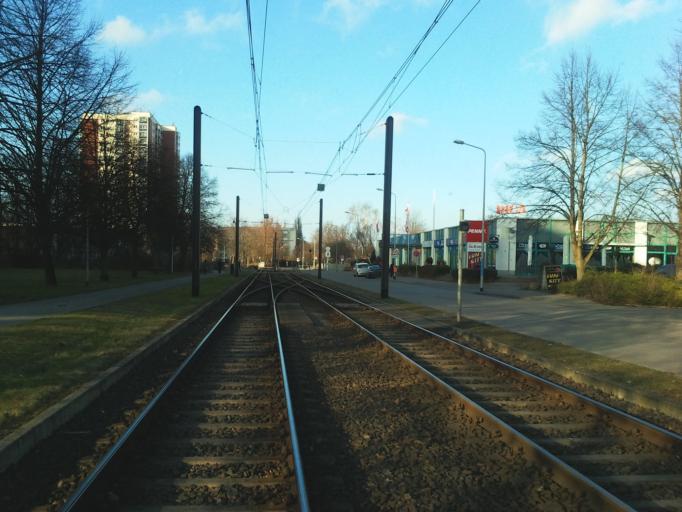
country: DE
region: Mecklenburg-Vorpommern
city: Elmenhorst
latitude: 54.1428
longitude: 12.0498
